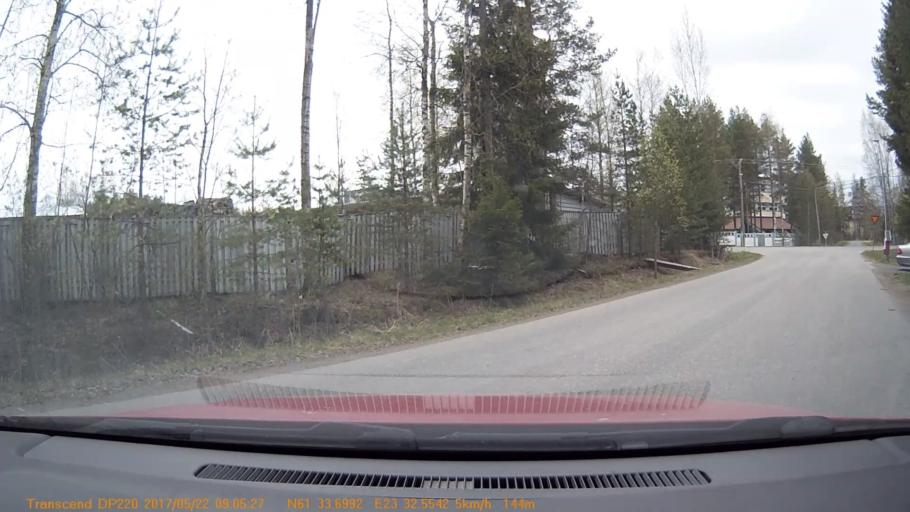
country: FI
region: Pirkanmaa
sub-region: Tampere
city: Yloejaervi
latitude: 61.5617
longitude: 23.5426
